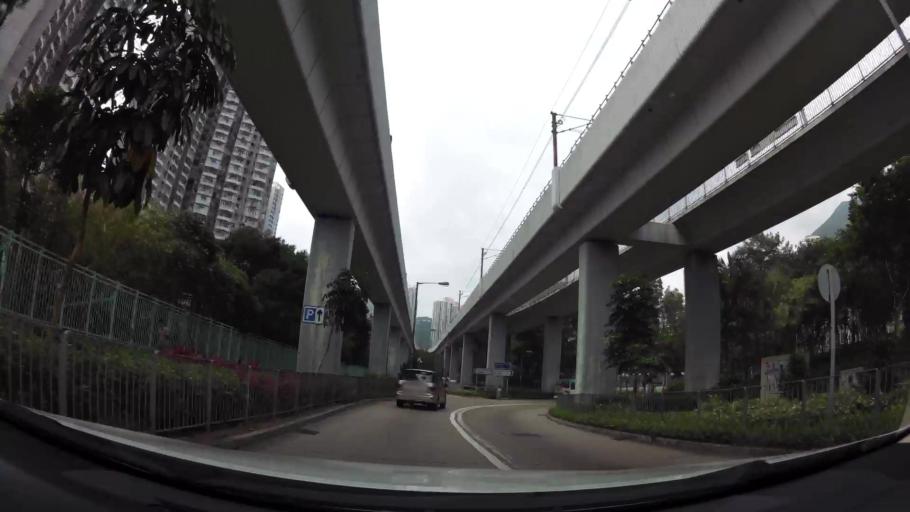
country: HK
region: Wanchai
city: Wan Chai
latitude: 22.2689
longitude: 114.2393
